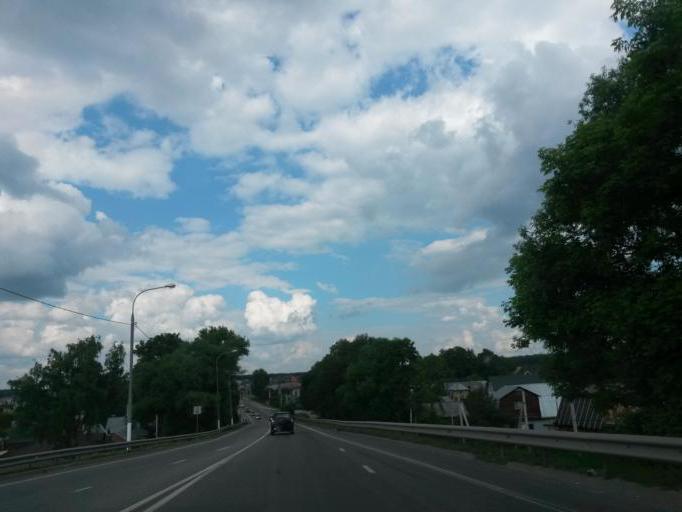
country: RU
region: Moskovskaya
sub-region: Chekhovskiy Rayon
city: Chekhov
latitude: 55.1803
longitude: 37.4878
